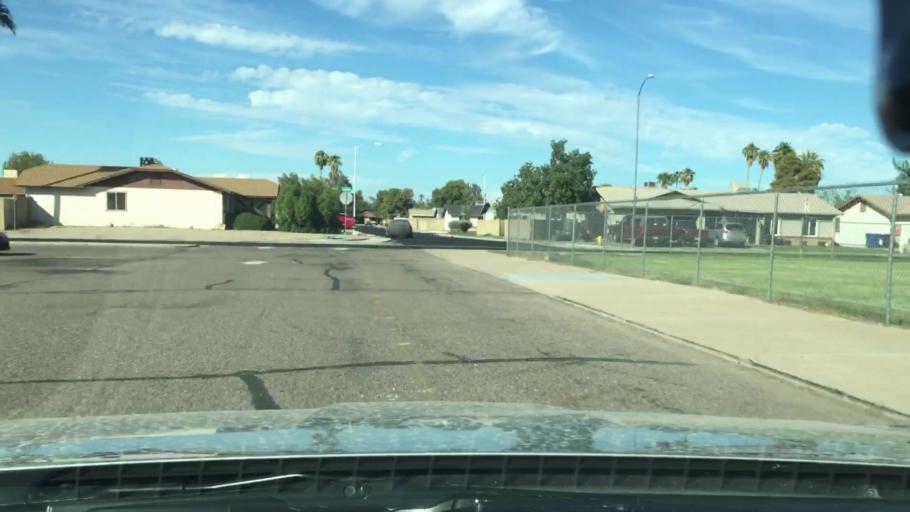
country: US
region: Arizona
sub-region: Maricopa County
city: Gilbert
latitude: 33.4041
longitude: -111.7610
